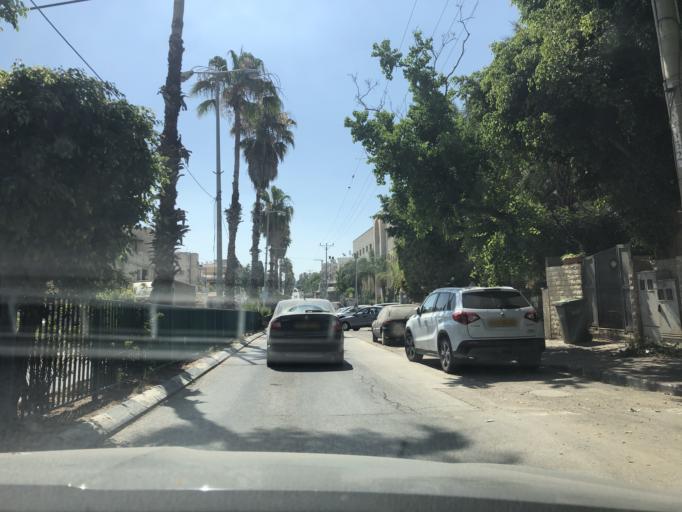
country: IL
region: Central District
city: Jaljulya
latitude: 32.1535
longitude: 34.9525
